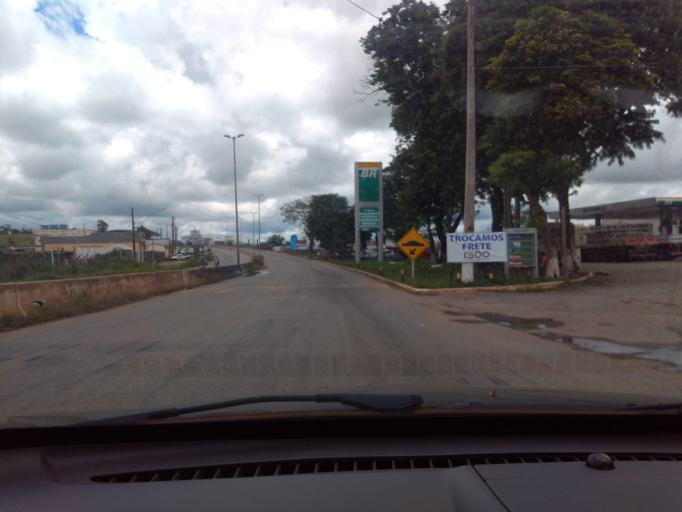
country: BR
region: Minas Gerais
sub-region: Lavras
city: Lavras
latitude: -21.2364
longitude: -45.0274
